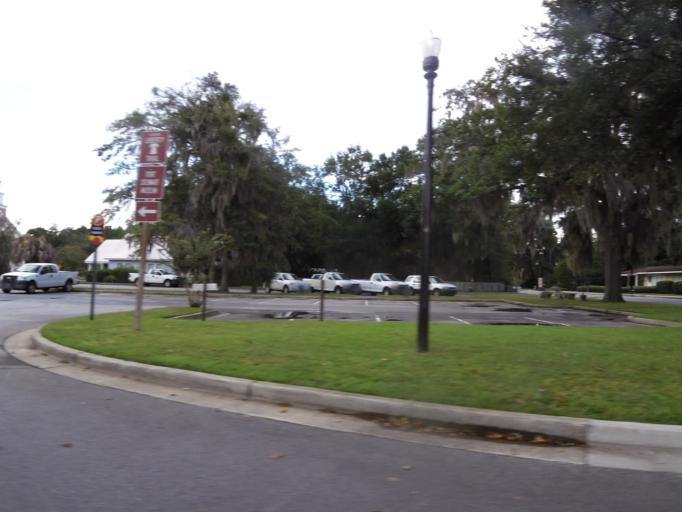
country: US
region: Georgia
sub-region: Liberty County
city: Hinesville
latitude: 31.8486
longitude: -81.5954
